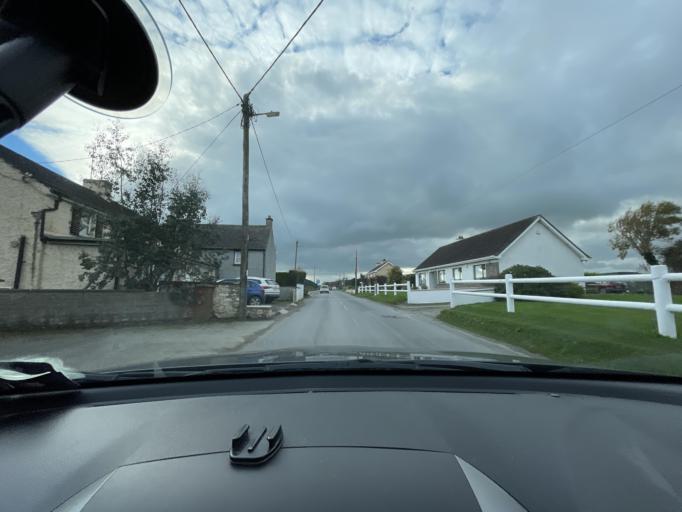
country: IE
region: Leinster
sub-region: Lu
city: Clogherhead
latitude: 53.7901
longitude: -6.2402
